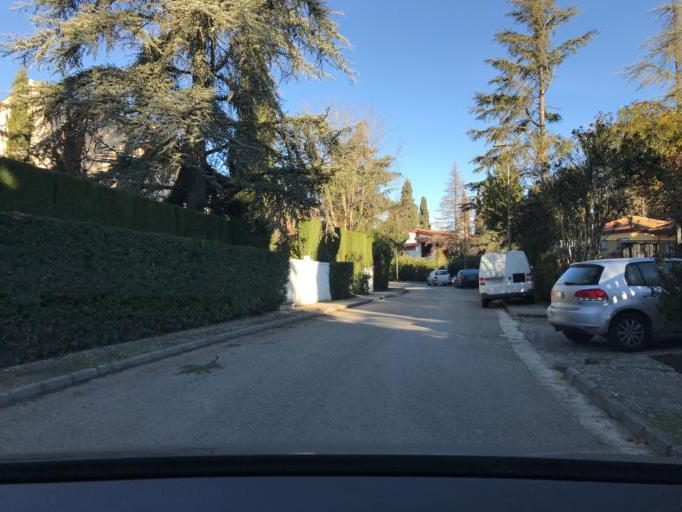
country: ES
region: Andalusia
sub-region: Provincia de Granada
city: Albolote
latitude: 37.2519
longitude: -3.6521
